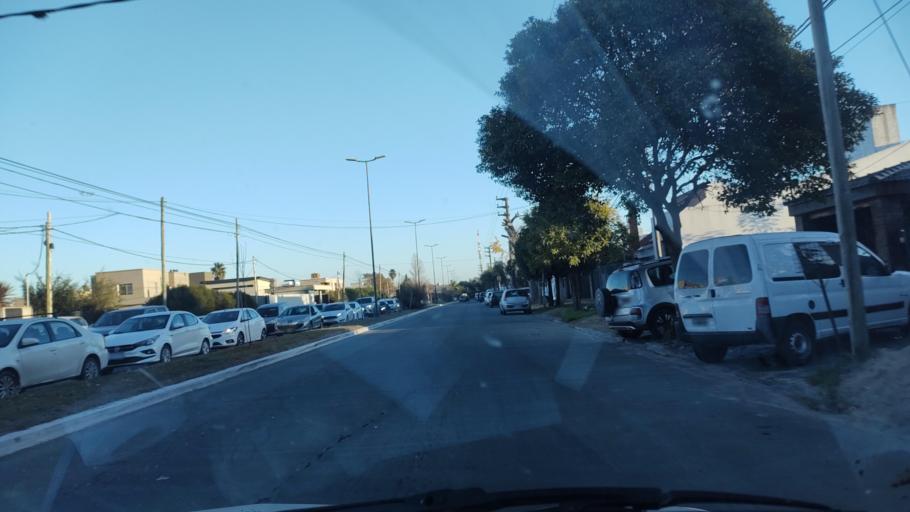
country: AR
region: Buenos Aires
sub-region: Partido de La Plata
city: La Plata
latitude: -34.8943
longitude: -58.0183
